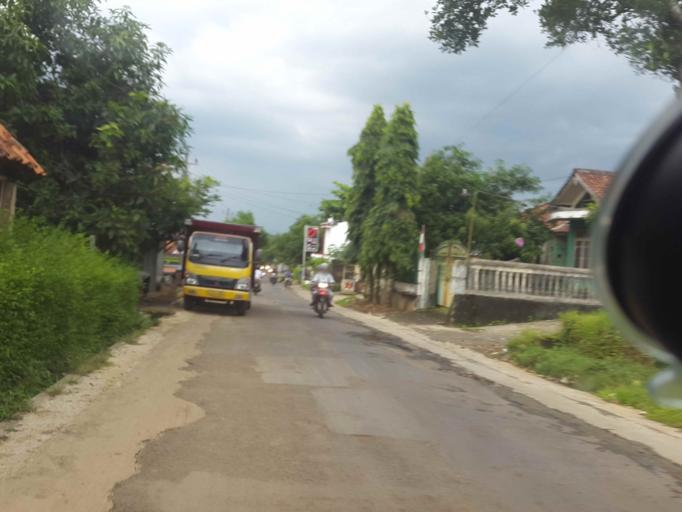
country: ID
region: Central Java
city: Banyumas
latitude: -7.5310
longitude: 109.3114
